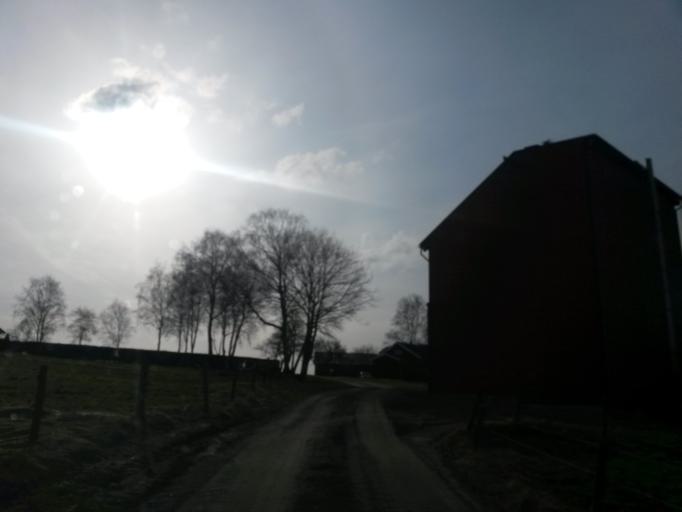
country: SE
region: Vaestra Goetaland
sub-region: Vargarda Kommun
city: Jonstorp
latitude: 57.9827
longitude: 12.6484
